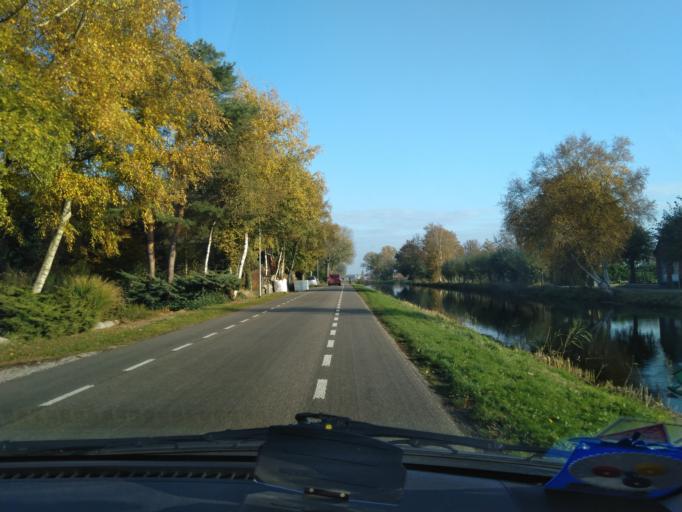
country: NL
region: Groningen
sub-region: Gemeente Hoogezand-Sappemeer
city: Sappemeer
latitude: 53.1635
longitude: 6.8223
